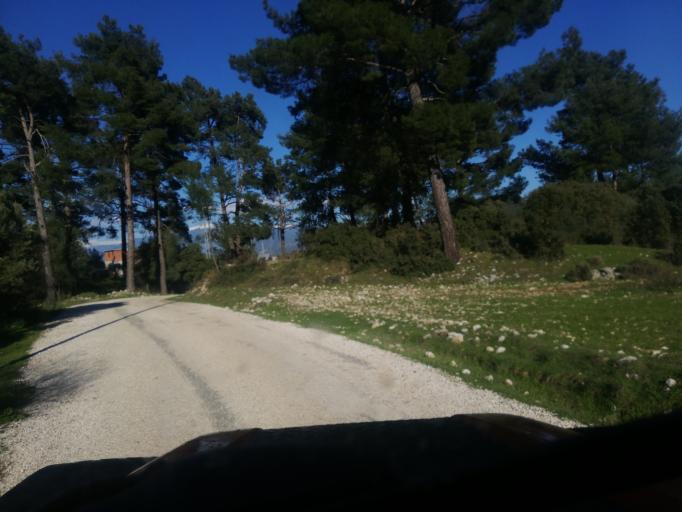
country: TR
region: Antalya
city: Kas
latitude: 36.2979
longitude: 29.6958
